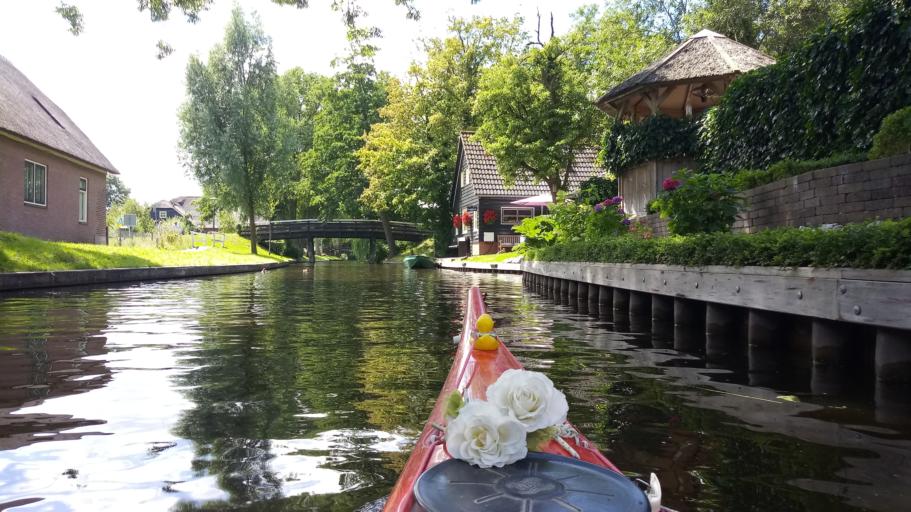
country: NL
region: Overijssel
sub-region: Gemeente Steenwijkerland
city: Giethoorn
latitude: 52.7106
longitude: 6.0807
